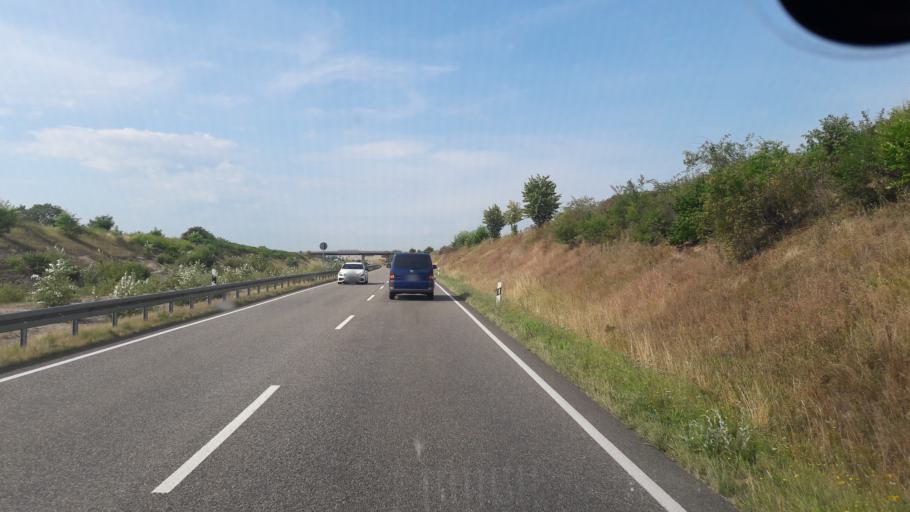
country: DE
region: Baden-Wuerttemberg
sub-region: Karlsruhe Region
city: Durmersheim
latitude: 48.9402
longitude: 8.2873
